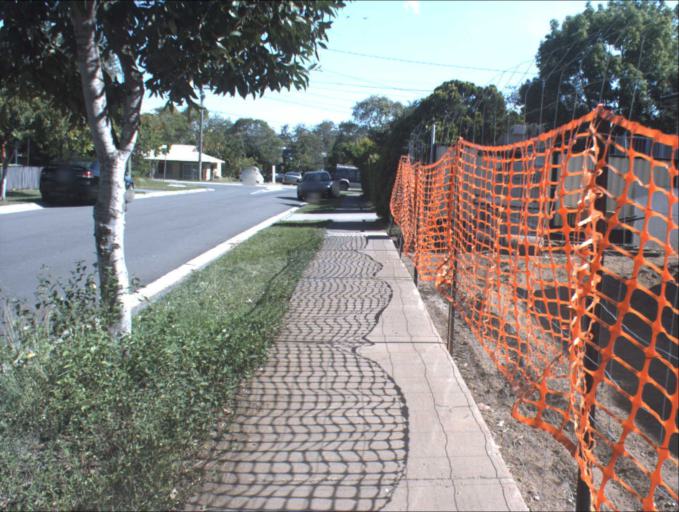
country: AU
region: Queensland
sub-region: Logan
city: Logan City
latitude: -27.6583
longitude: 153.1109
